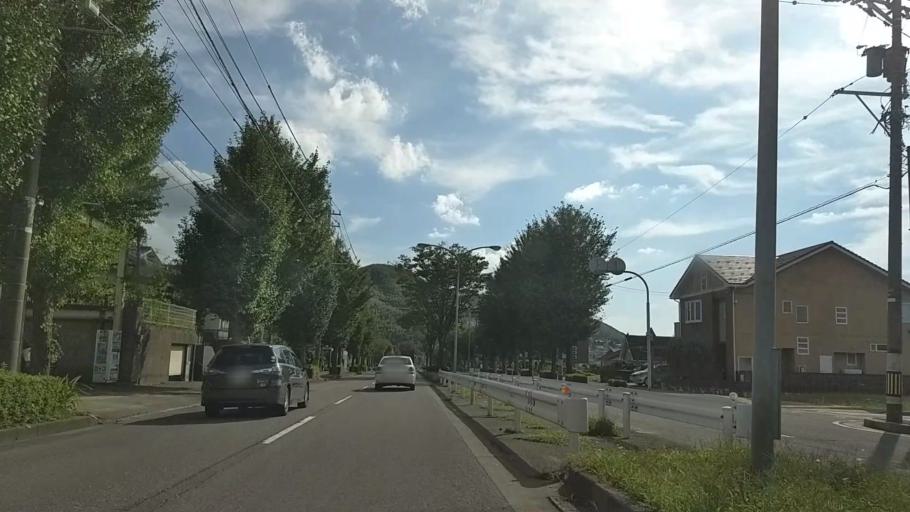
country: JP
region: Ishikawa
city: Nonoichi
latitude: 36.5321
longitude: 136.6534
